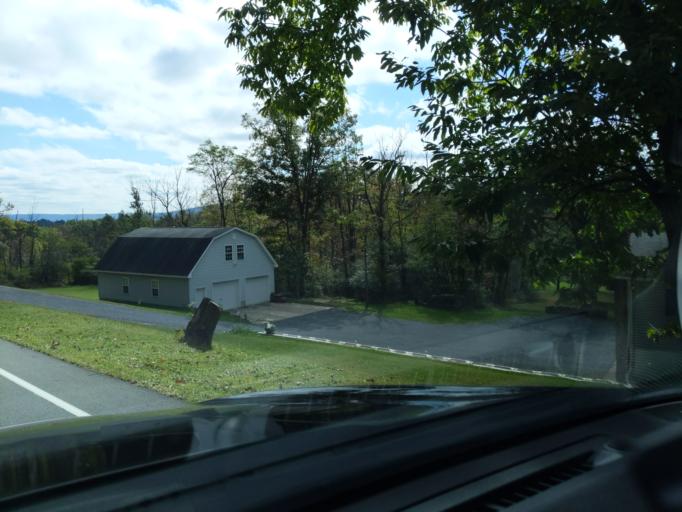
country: US
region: Pennsylvania
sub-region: Blair County
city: Lakemont
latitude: 40.4892
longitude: -78.4363
